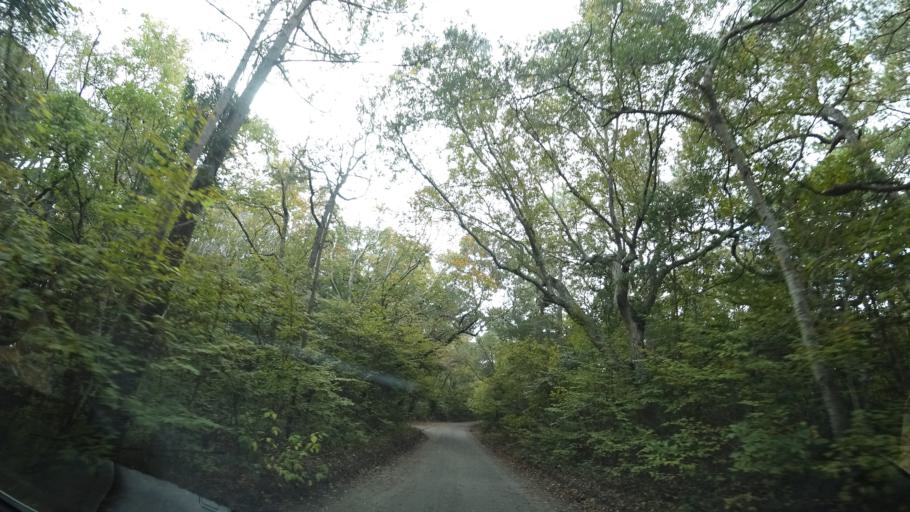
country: US
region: North Carolina
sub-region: Dare County
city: Kill Devil Hills
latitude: 35.9996
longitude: -75.6652
